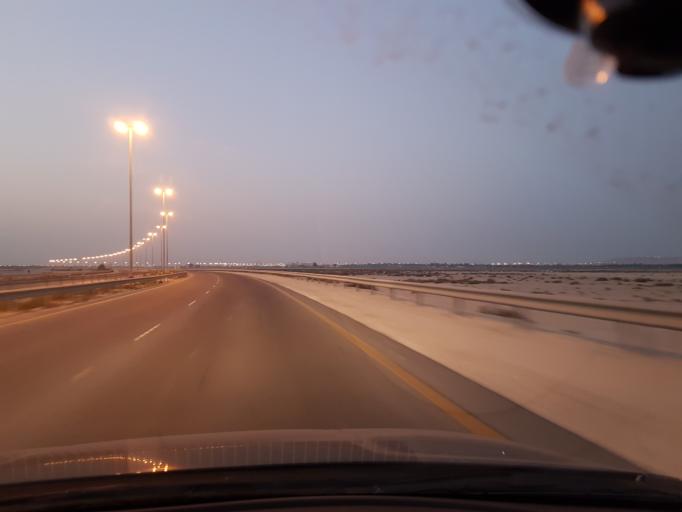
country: BH
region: Central Governorate
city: Dar Kulayb
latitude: 25.9986
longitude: 50.4850
